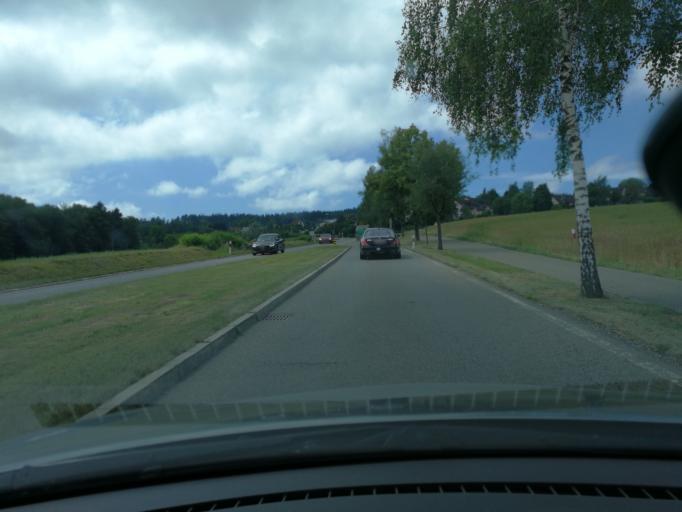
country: CH
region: Zurich
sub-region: Bezirk Uster
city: Binz
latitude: 47.3613
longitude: 8.6300
